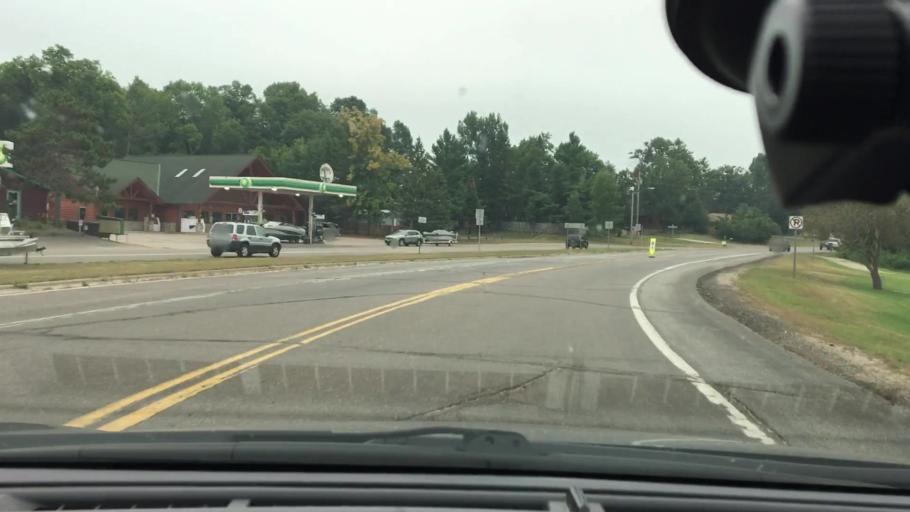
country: US
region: Minnesota
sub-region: Crow Wing County
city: Cross Lake
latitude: 46.8188
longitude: -93.9433
